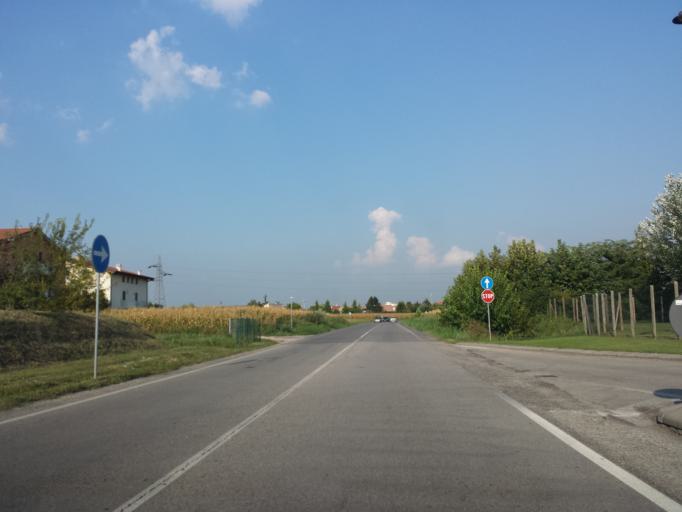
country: IT
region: Veneto
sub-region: Provincia di Vicenza
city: Torri di Quartesolo
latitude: 45.5146
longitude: 11.6294
